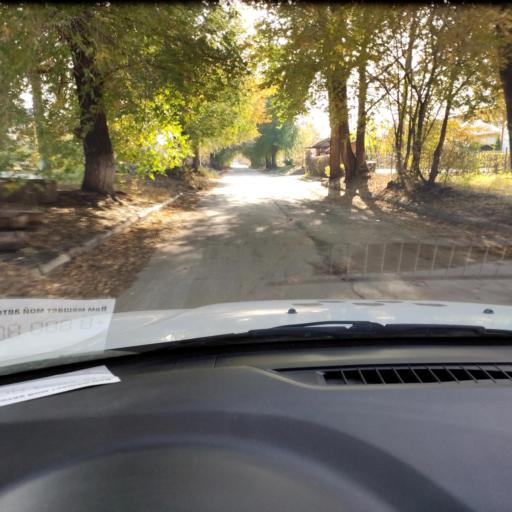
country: RU
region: Samara
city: Tol'yatti
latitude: 53.5342
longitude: 49.4048
